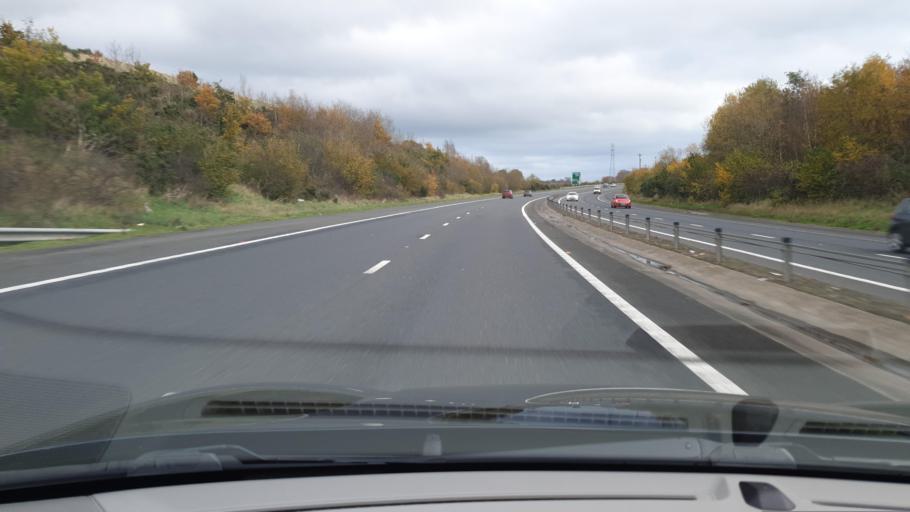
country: GB
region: Northern Ireland
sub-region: Newry and Mourne District
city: Newry
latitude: 54.2138
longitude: -6.3523
